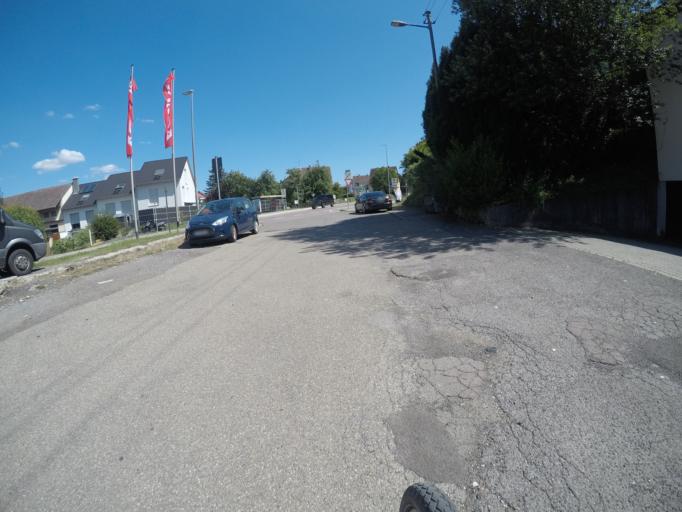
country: DE
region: Baden-Wuerttemberg
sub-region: Regierungsbezirk Stuttgart
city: Leinfelden-Echterdingen
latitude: 48.7034
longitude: 9.2050
